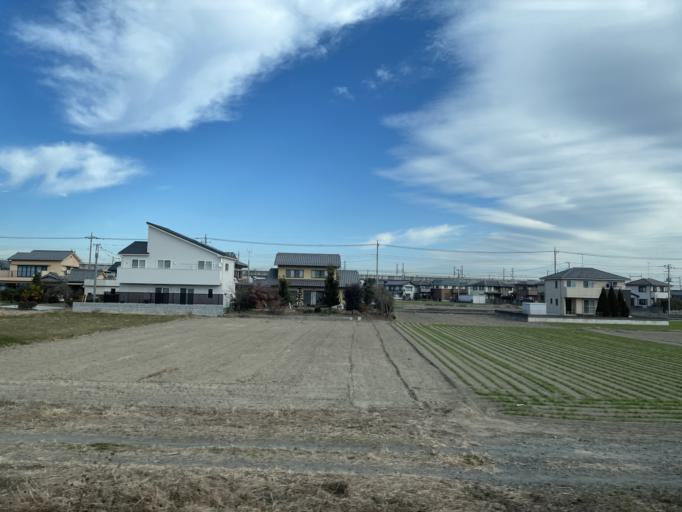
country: JP
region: Saitama
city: Kumagaya
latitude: 36.1309
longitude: 139.4042
